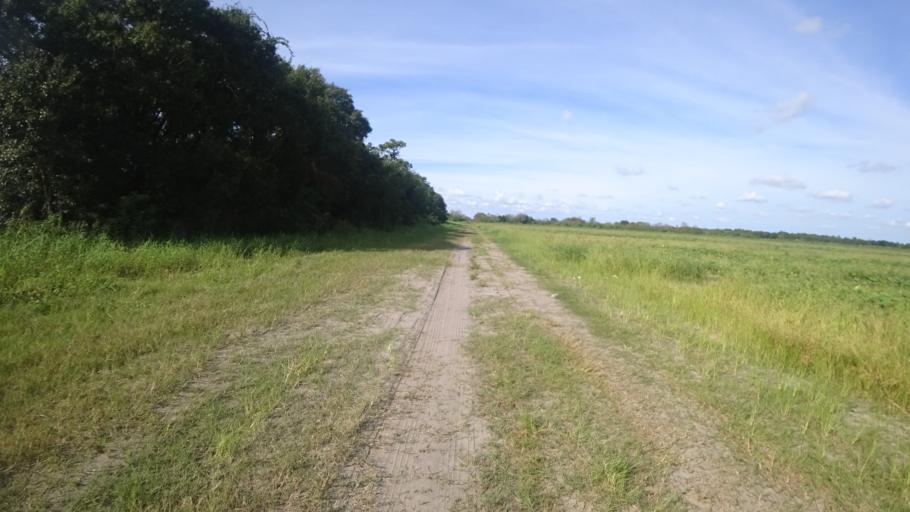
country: US
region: Florida
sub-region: Sarasota County
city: The Meadows
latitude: 27.4484
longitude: -82.3157
